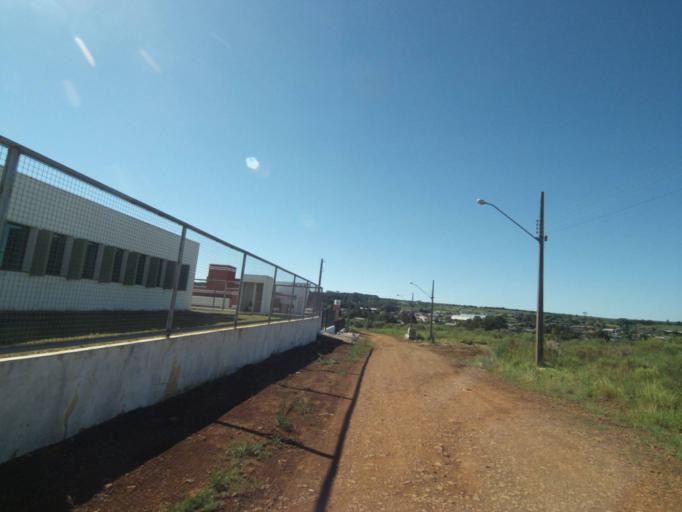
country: BR
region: Parana
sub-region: Pinhao
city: Pinhao
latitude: -25.8360
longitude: -52.0321
